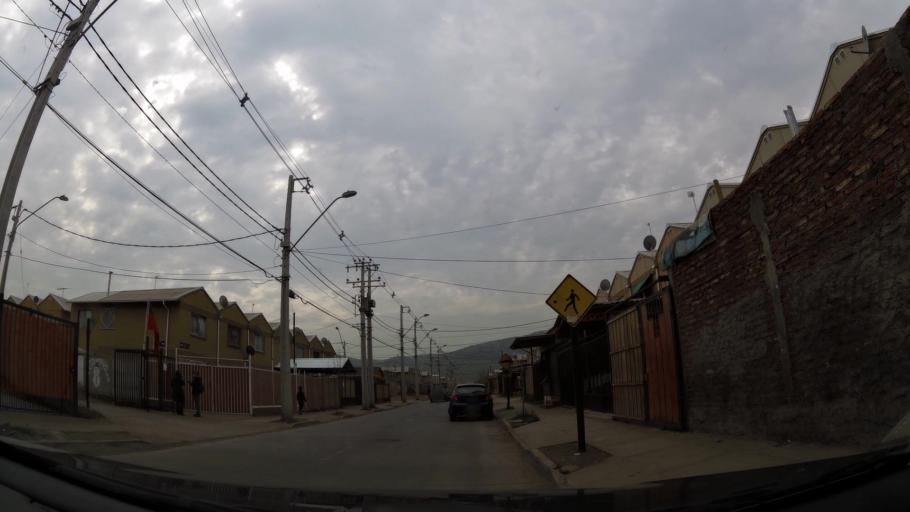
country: CL
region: Santiago Metropolitan
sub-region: Provincia de Chacabuco
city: Chicureo Abajo
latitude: -33.1868
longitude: -70.6674
